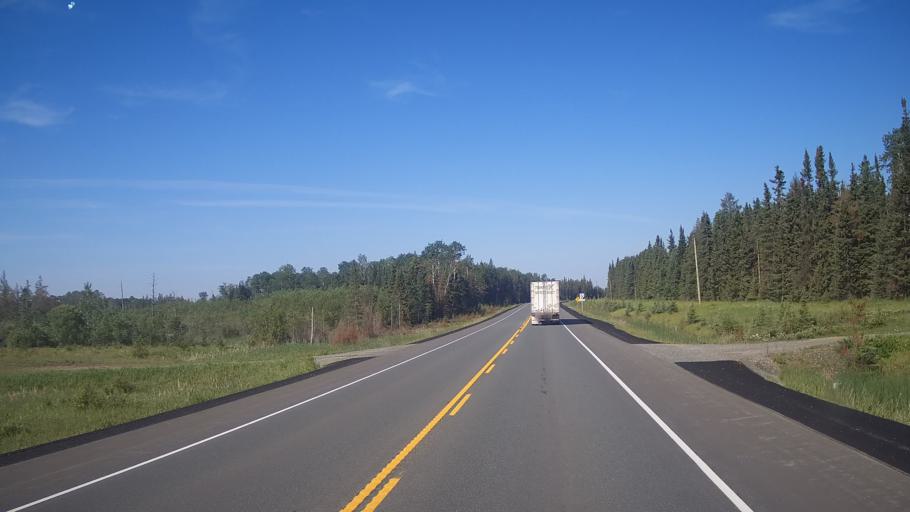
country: CA
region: Ontario
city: Dryden
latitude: 49.5855
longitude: -92.2965
